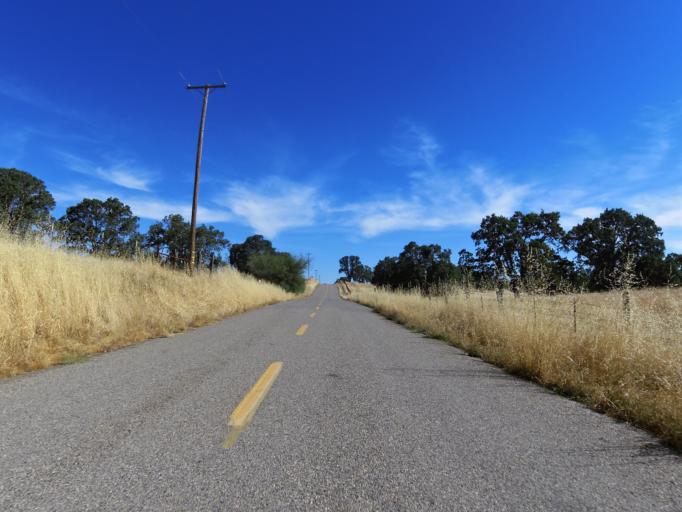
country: US
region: California
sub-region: Madera County
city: Yosemite Lakes
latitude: 37.2508
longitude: -119.9250
